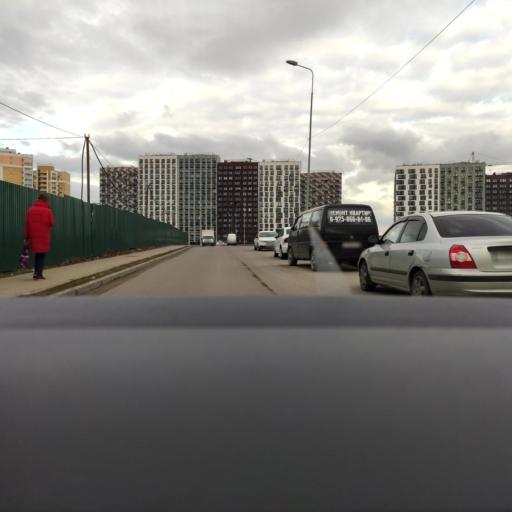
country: RU
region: Moskovskaya
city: Vidnoye
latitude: 55.5321
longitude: 37.7189
